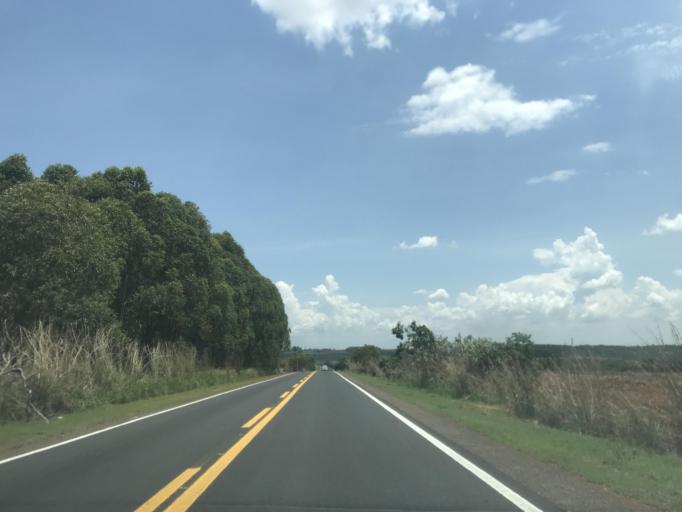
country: BR
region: Goias
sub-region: Bela Vista De Goias
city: Bela Vista de Goias
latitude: -17.1125
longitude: -48.6664
